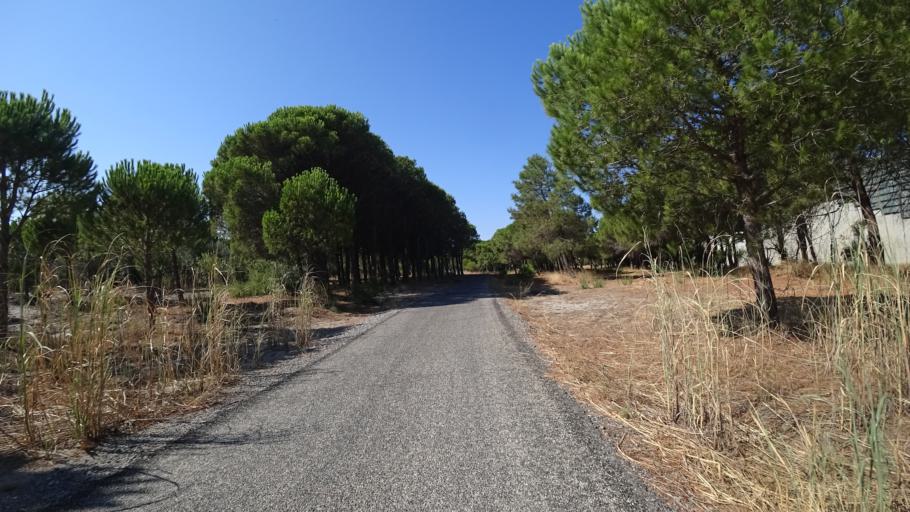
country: FR
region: Languedoc-Roussillon
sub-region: Departement de l'Aude
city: Leucate
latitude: 42.8657
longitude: 3.0326
